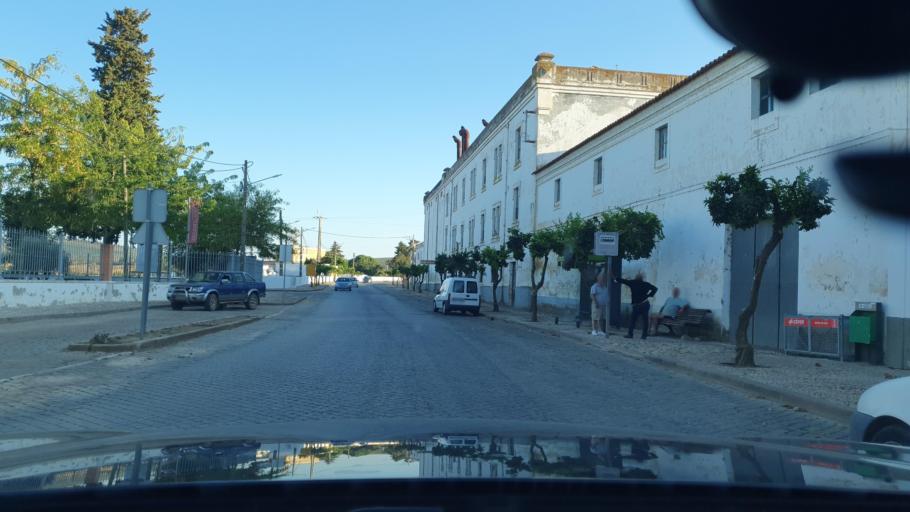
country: PT
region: Portalegre
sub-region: Fronteira
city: Fronteira
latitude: 38.9501
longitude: -7.6759
